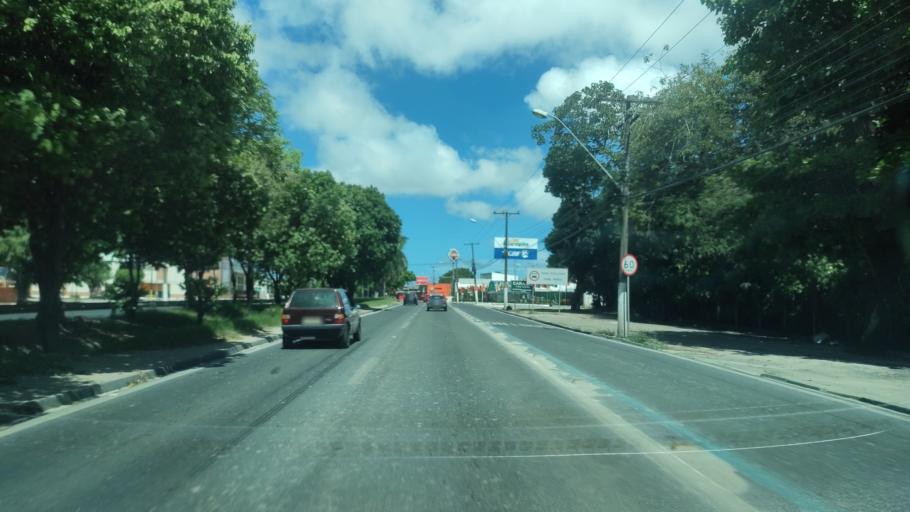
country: BR
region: Alagoas
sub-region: Satuba
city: Satuba
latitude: -9.5887
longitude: -35.7615
